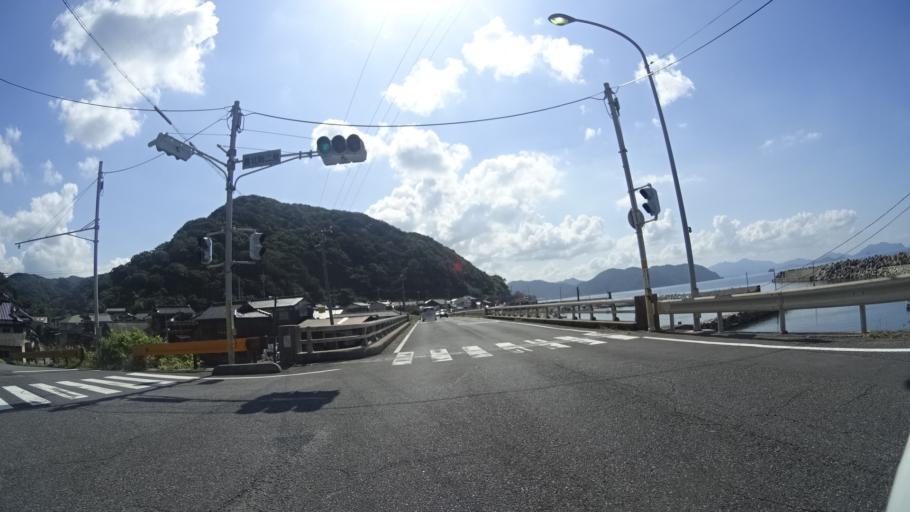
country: JP
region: Yamaguchi
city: Shimonoseki
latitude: 34.2498
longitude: 130.9079
